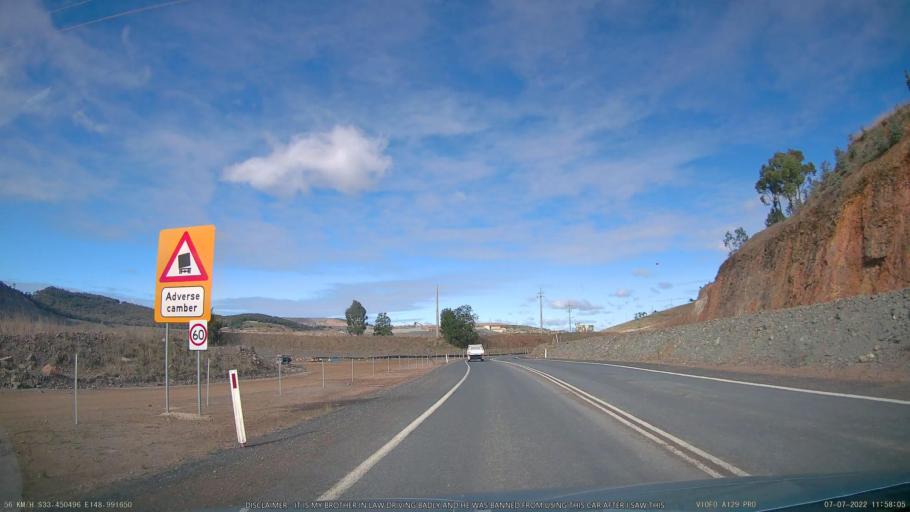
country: AU
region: New South Wales
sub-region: Blayney
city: Millthorpe
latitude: -33.4508
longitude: 148.9917
